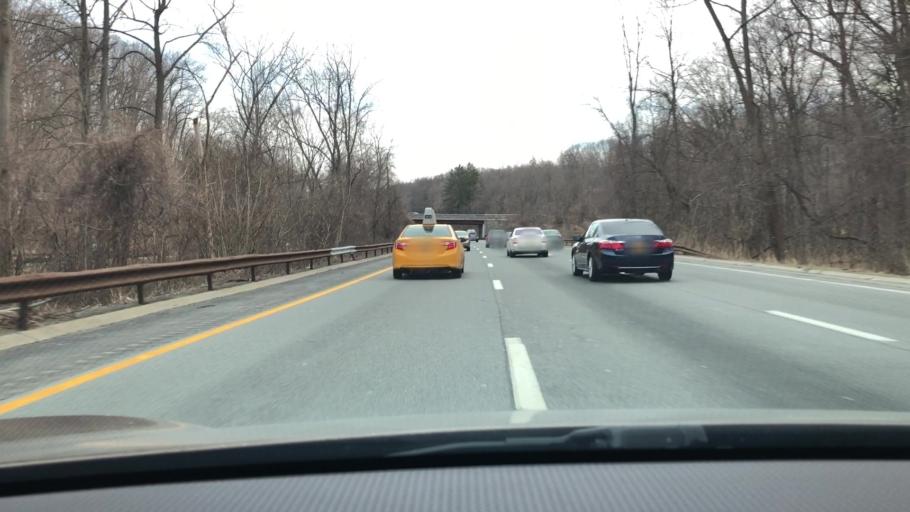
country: US
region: New York
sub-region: Westchester County
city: Greenville
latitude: 40.9977
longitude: -73.8330
